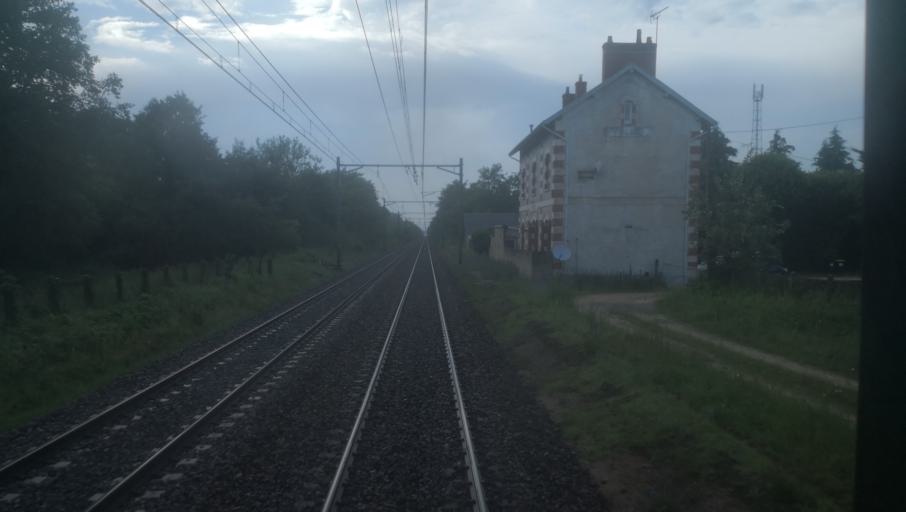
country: FR
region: Centre
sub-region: Departement du Loiret
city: Menestreau-en-Villette
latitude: 47.6503
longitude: 1.9823
